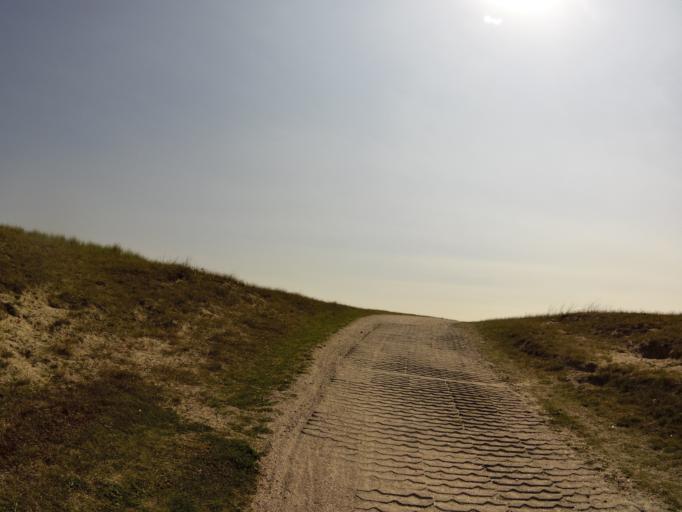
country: NL
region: North Holland
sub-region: Gemeente Schagen
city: Harenkarspel
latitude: 52.7841
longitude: 4.6721
